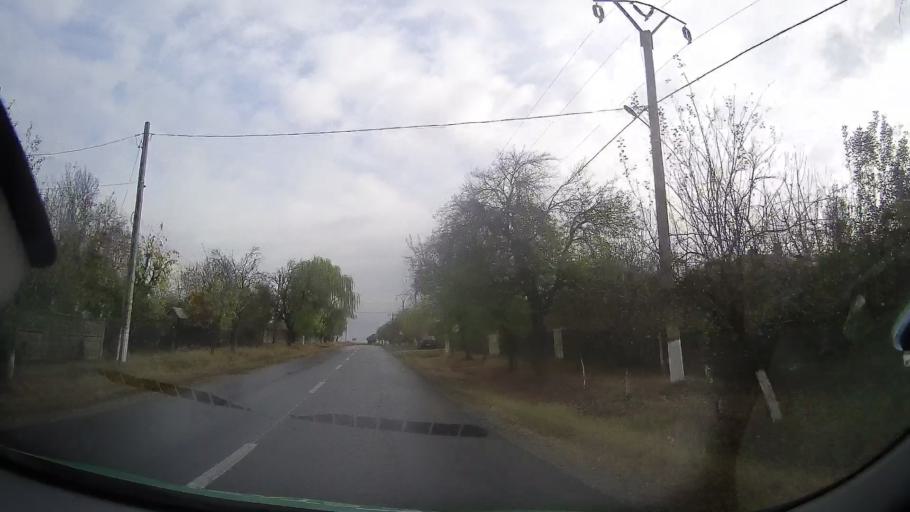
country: RO
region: Ialomita
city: Brazii
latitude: 44.7579
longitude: 26.3684
